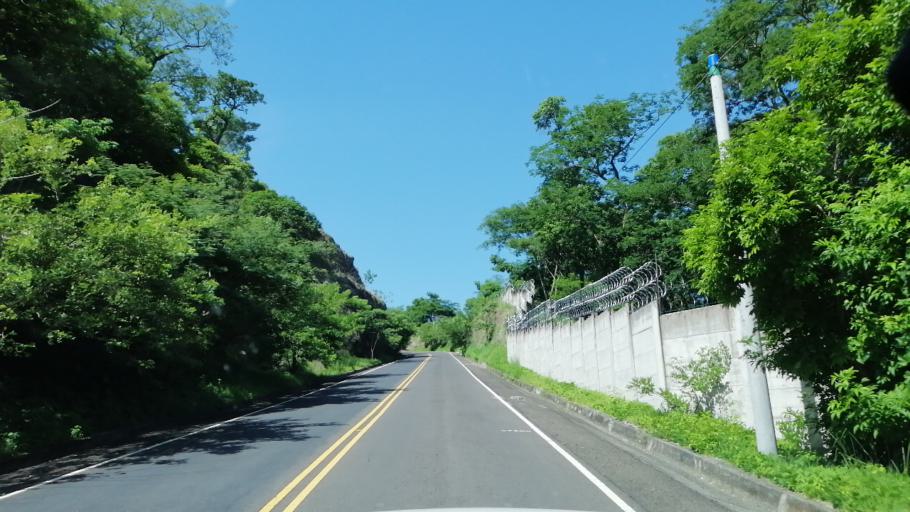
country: HN
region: Lempira
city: La Virtud
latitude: 13.9840
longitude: -88.7579
